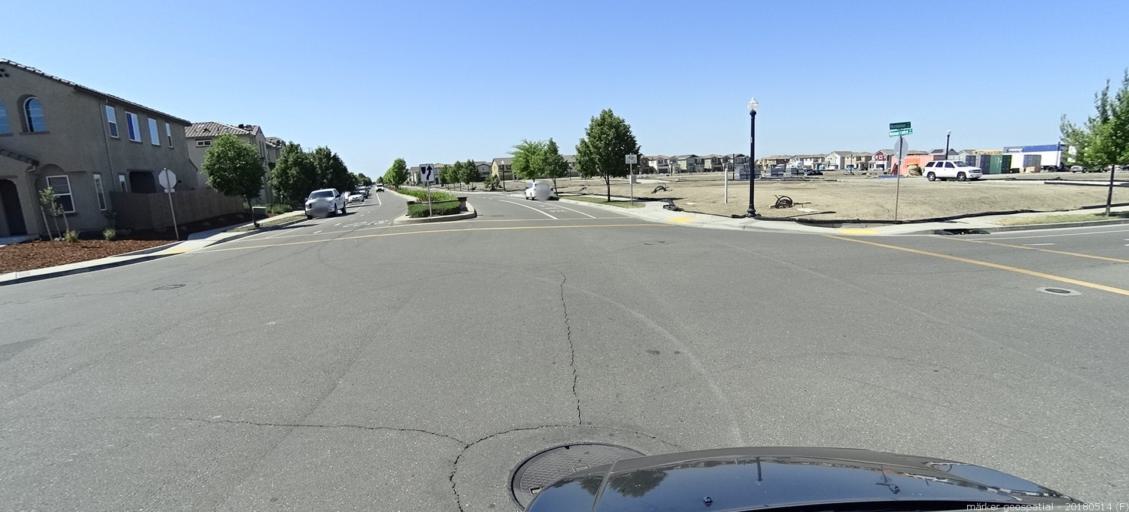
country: US
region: California
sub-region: Yolo County
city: West Sacramento
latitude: 38.6526
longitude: -121.5441
